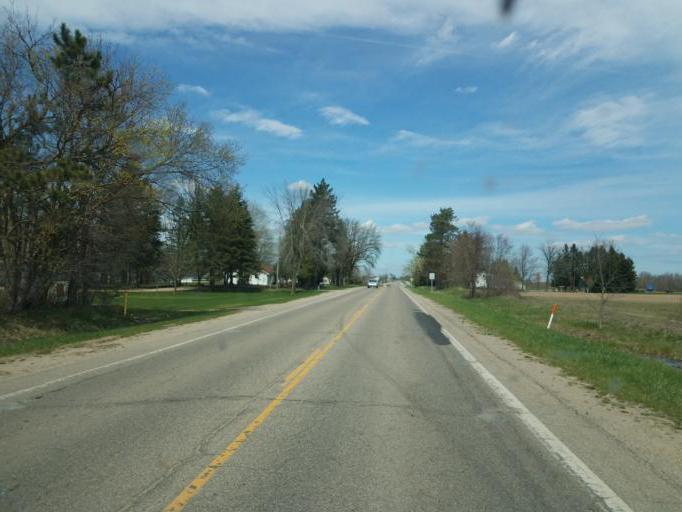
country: US
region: Michigan
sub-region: Isabella County
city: Mount Pleasant
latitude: 43.6364
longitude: -84.7681
